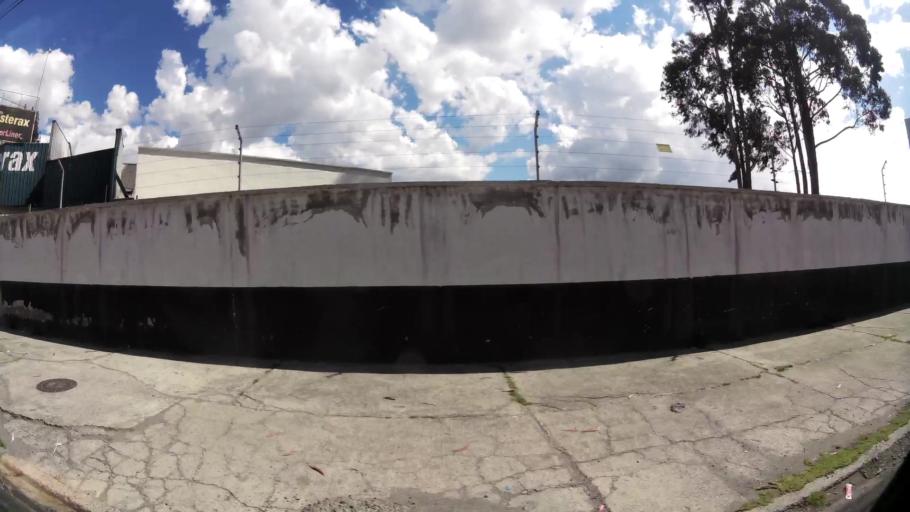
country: EC
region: Pichincha
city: Quito
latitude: -0.1160
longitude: -78.4743
